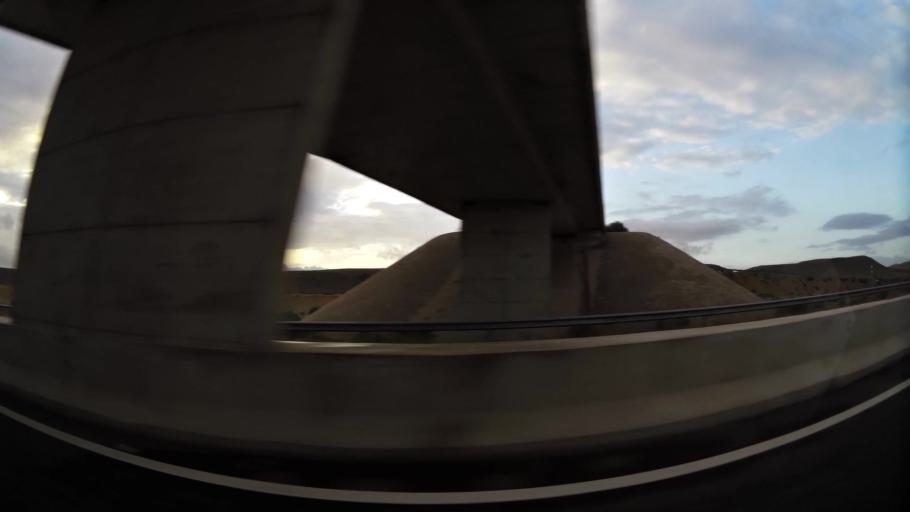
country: MA
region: Oriental
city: Taourirt
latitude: 34.4457
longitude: -3.0595
